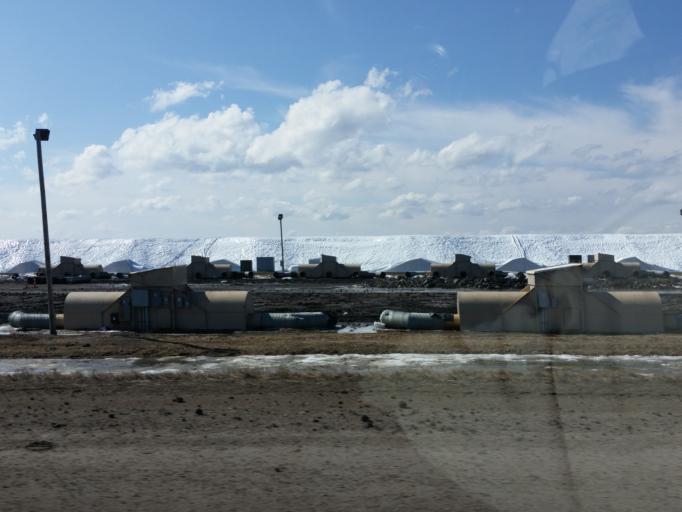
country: US
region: North Dakota
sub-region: Walsh County
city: Grafton
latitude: 48.2149
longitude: -97.3625
